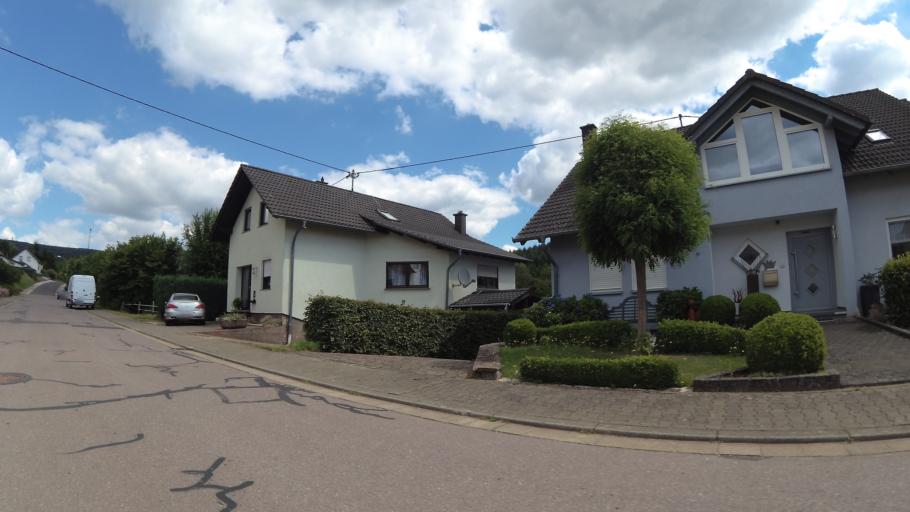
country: DE
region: Saarland
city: Weiskirchen
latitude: 49.5641
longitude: 6.8203
